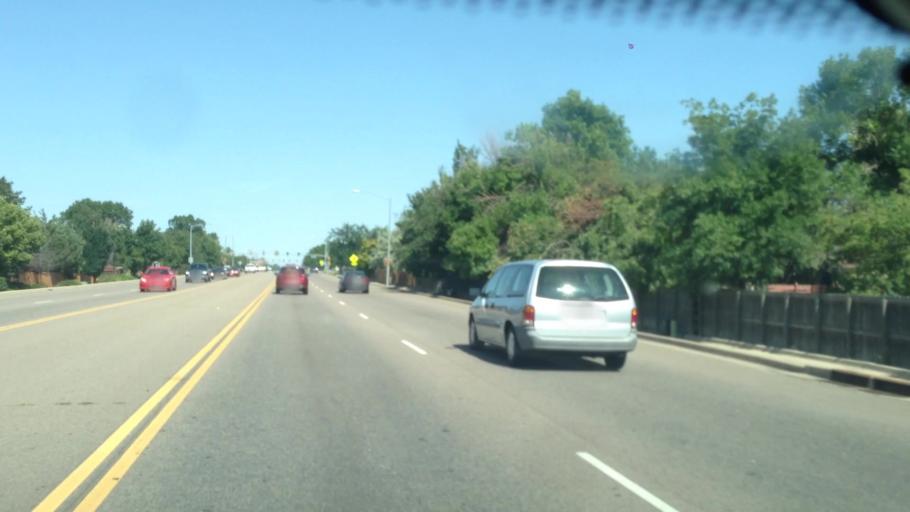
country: US
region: Colorado
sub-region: Adams County
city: Aurora
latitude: 39.7256
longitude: -104.8543
